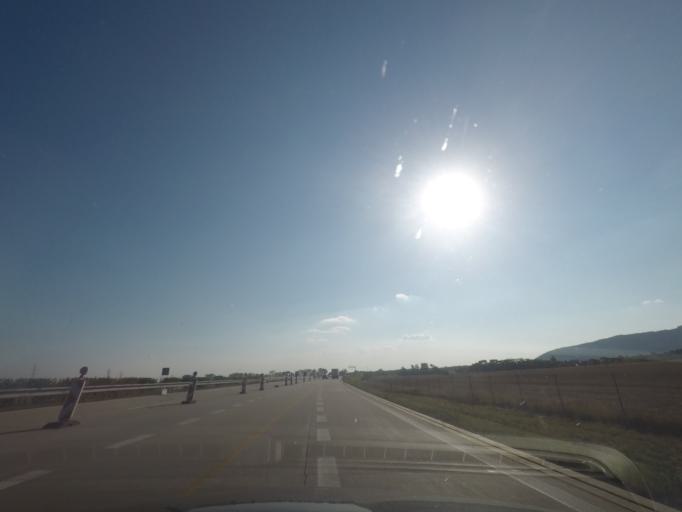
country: CZ
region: Olomoucky
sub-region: Okres Prerov
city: Lipnik nad Becvou
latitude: 49.5494
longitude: 17.6012
